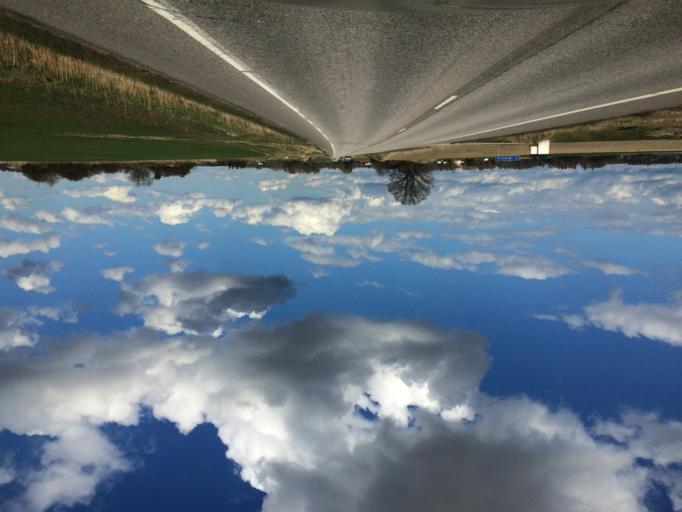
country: SE
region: Soedermanland
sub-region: Eskilstuna Kommun
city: Eskilstuna
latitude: 59.4153
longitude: 16.5871
